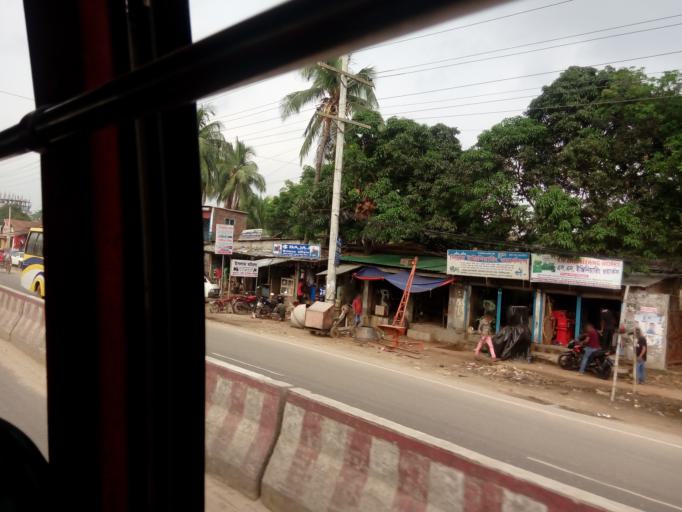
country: BD
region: Dhaka
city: Tungi
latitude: 23.9405
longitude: 90.2708
